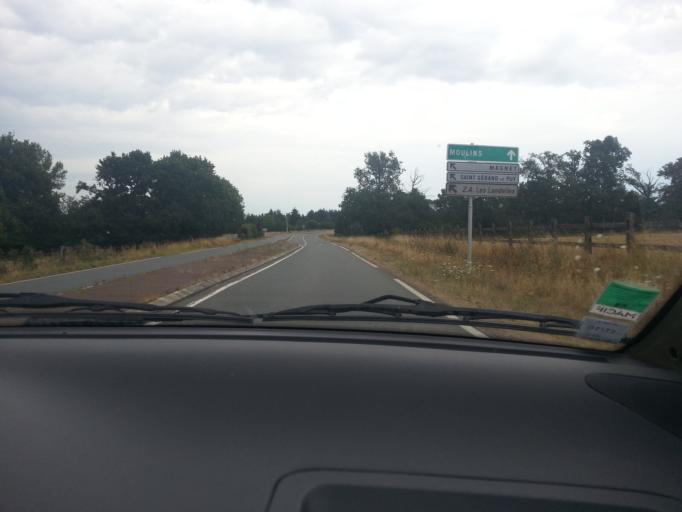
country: FR
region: Auvergne
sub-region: Departement de l'Allier
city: Saint-Gerand-le-Puy
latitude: 46.2058
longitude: 3.5002
